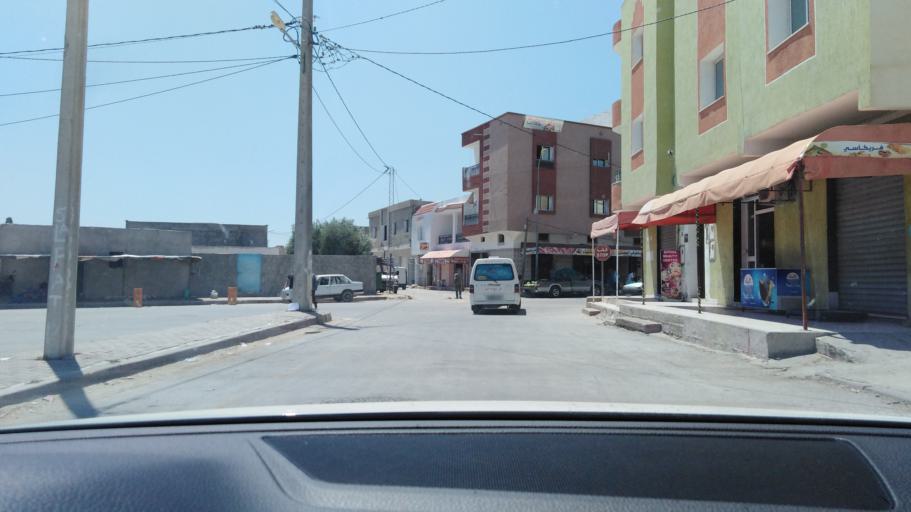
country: TN
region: Al Qayrawan
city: Sbikha
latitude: 36.1170
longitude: 10.0949
